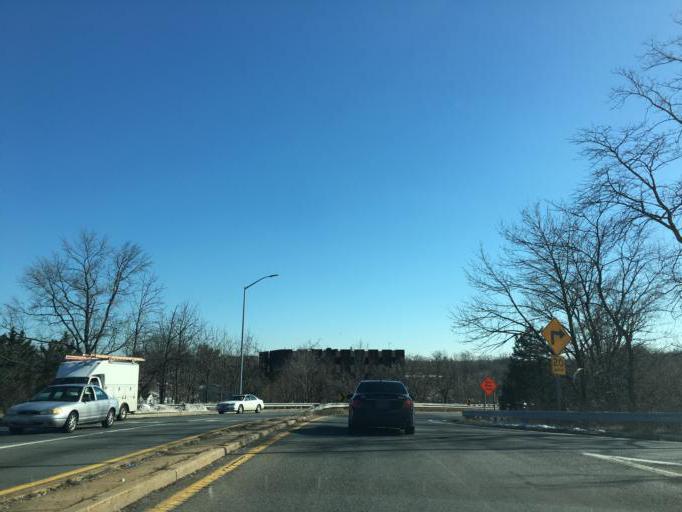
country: US
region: Maryland
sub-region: Baltimore County
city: Lansdowne
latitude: 39.2455
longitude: -76.6728
